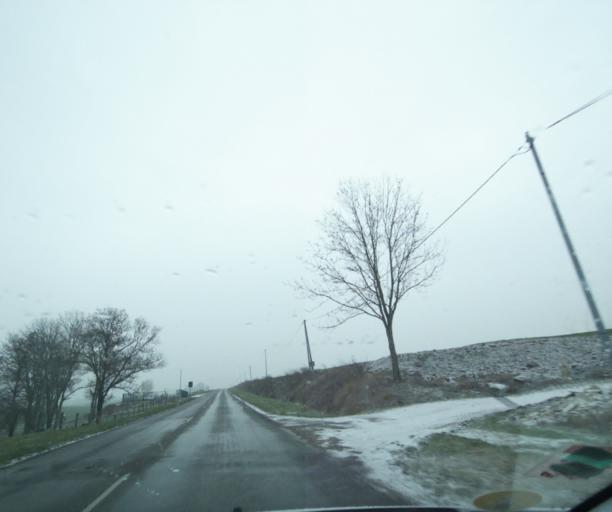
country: FR
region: Champagne-Ardenne
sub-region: Departement de la Haute-Marne
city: Wassy
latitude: 48.4884
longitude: 4.9745
